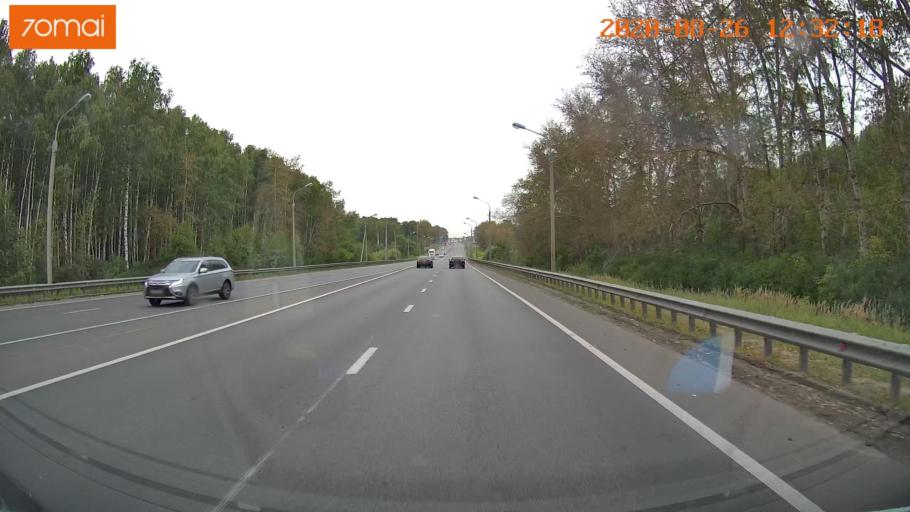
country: RU
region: Rjazan
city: Ryazan'
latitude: 54.5764
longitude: 39.7927
